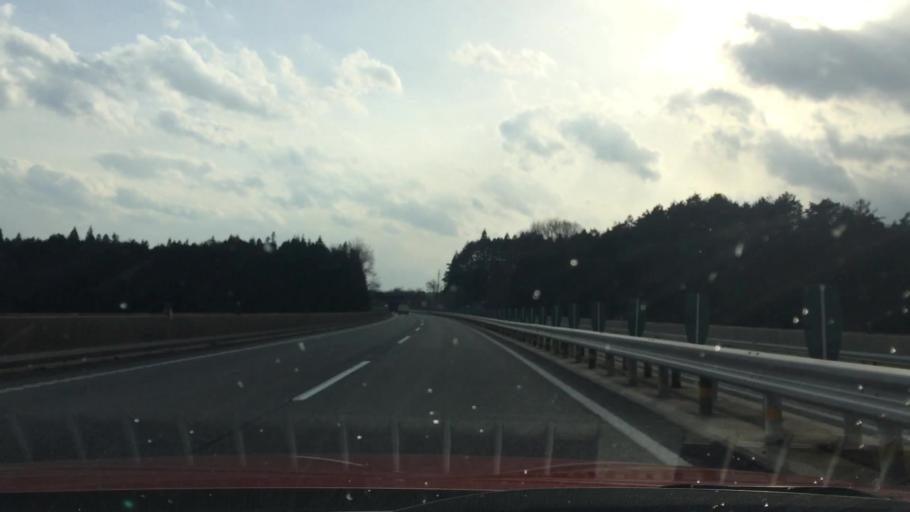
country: JP
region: Nagano
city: Ina
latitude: 35.6717
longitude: 137.9047
